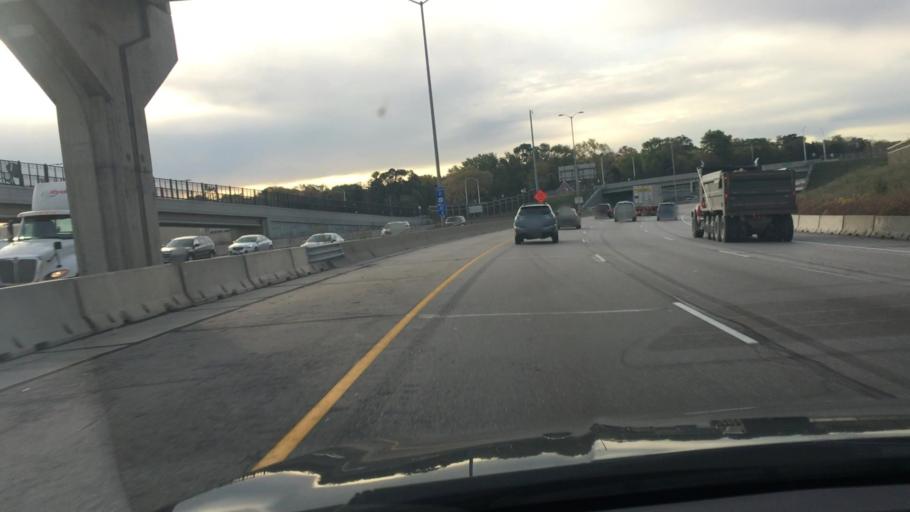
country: US
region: Wisconsin
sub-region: Waukesha County
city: Elm Grove
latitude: 43.0695
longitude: -88.0544
